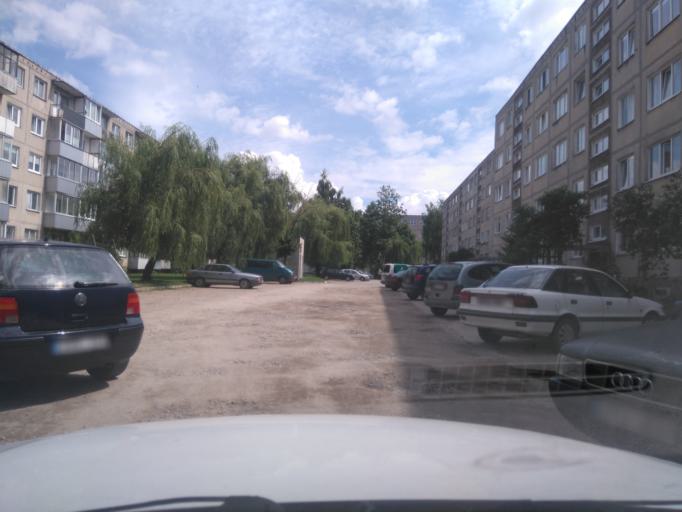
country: LT
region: Marijampoles apskritis
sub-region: Marijampole Municipality
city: Marijampole
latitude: 54.5694
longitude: 23.3506
